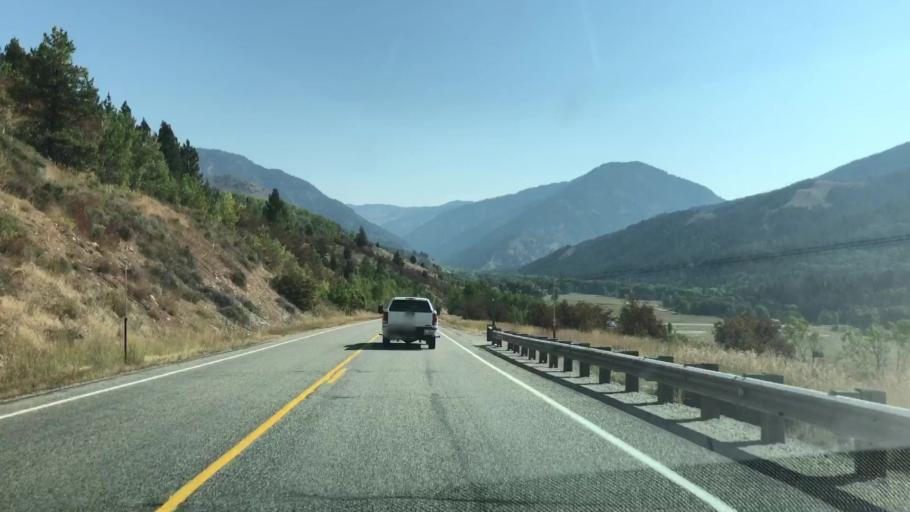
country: US
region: Wyoming
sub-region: Teton County
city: Hoback
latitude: 43.2510
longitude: -111.1124
